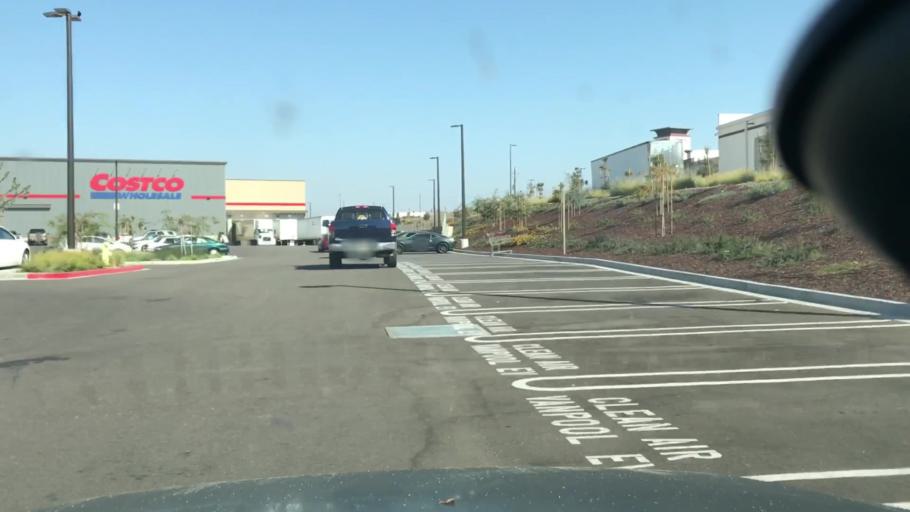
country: US
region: California
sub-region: Santa Barbara County
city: Santa Maria
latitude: 34.9262
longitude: -120.4208
